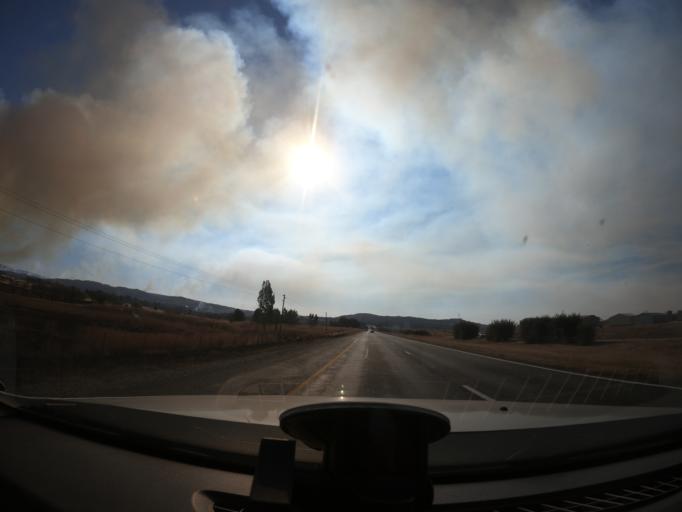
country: ZA
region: Gauteng
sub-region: Sedibeng District Municipality
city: Heidelberg
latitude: -26.5103
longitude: 28.3861
